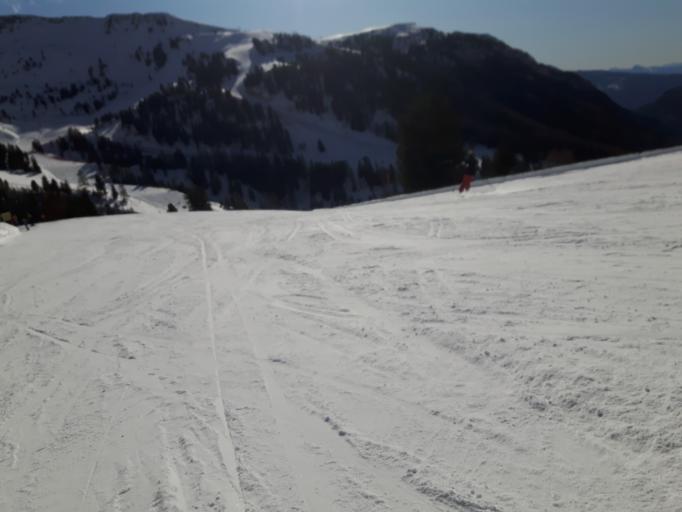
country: IT
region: Trentino-Alto Adige
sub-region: Provincia di Trento
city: Predazzo
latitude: 46.3468
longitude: 11.5511
